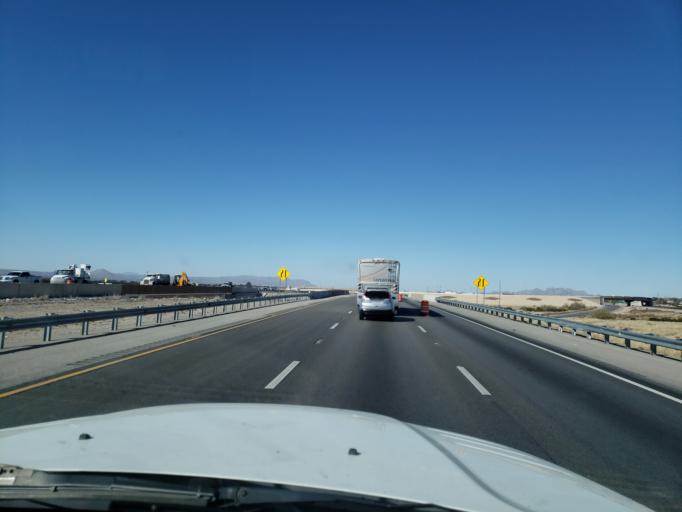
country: US
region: New Mexico
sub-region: Dona Ana County
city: University Park
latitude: 32.2582
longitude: -106.7302
